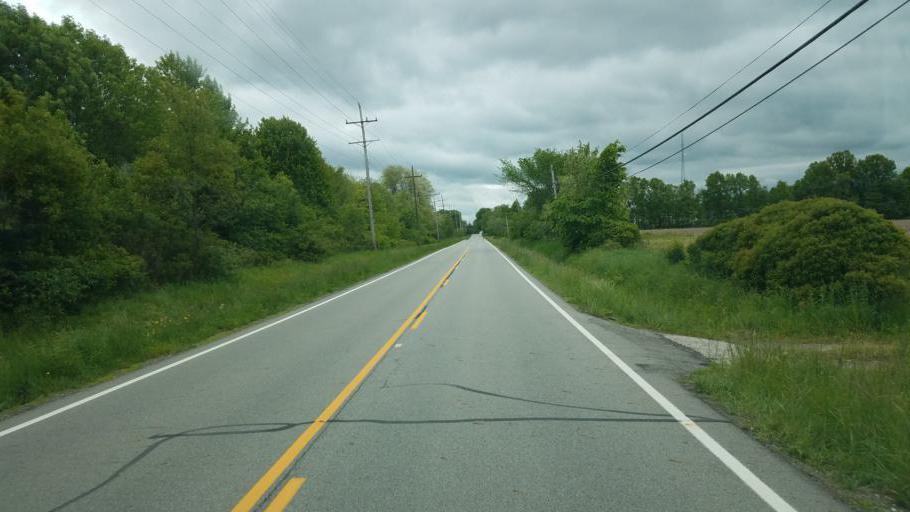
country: US
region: Ohio
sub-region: Geauga County
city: Burton
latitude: 41.3981
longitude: -81.1717
